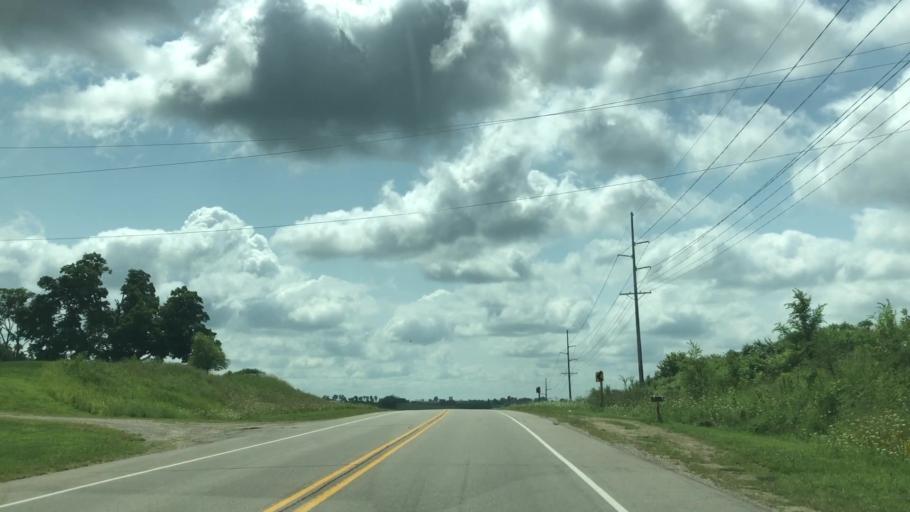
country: US
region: Iowa
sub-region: Marshall County
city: Marshalltown
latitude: 42.0264
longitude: -92.9604
